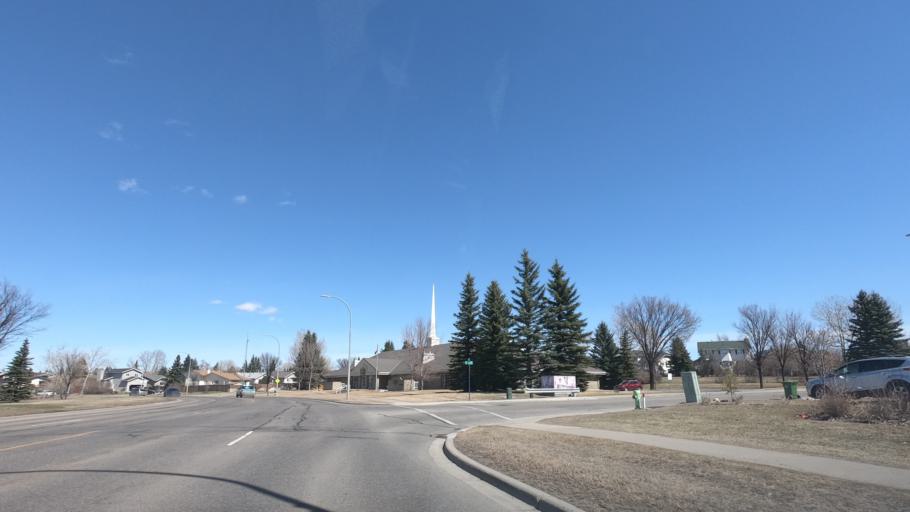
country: CA
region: Alberta
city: Airdrie
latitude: 51.2793
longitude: -114.0085
